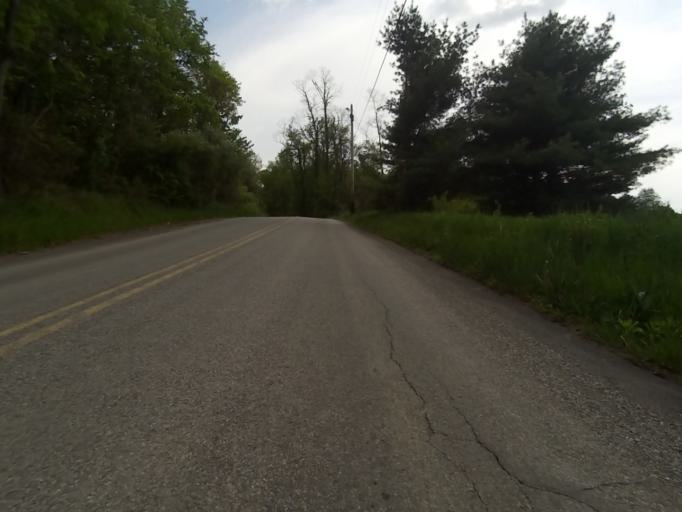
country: US
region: Pennsylvania
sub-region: Centre County
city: Zion
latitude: 40.9766
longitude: -77.6263
